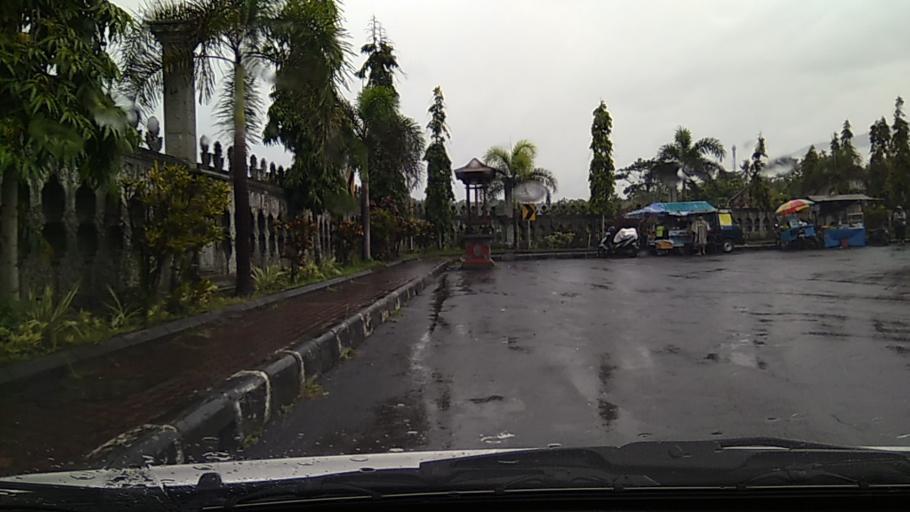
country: ID
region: Bali
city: Banjar Danginsema
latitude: -8.4643
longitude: 115.6317
